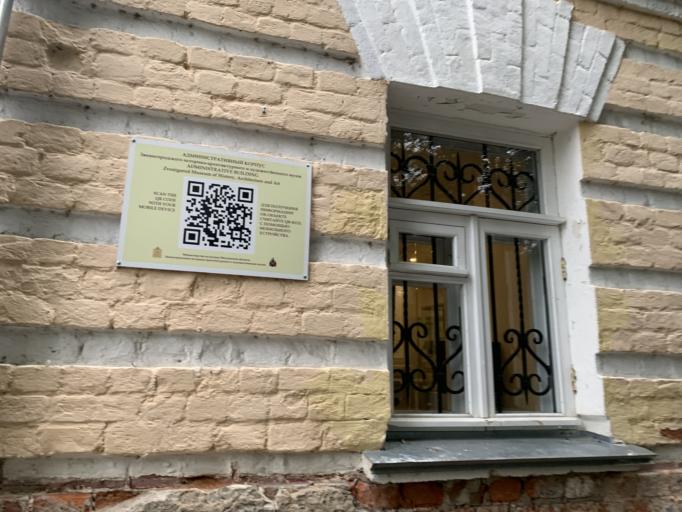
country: RU
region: Moskovskaya
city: Zvenigorod
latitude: 55.7300
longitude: 36.8155
